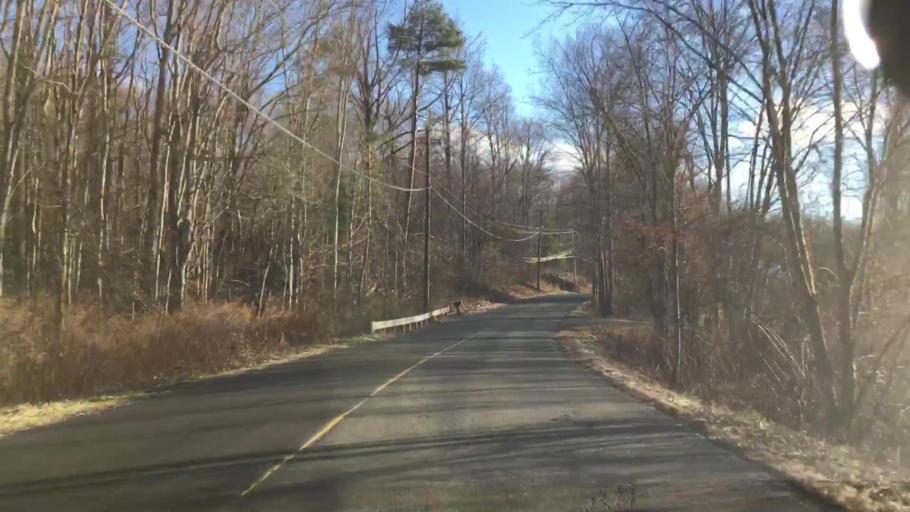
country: US
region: Connecticut
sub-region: Fairfield County
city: Newtown
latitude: 41.4393
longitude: -73.3147
